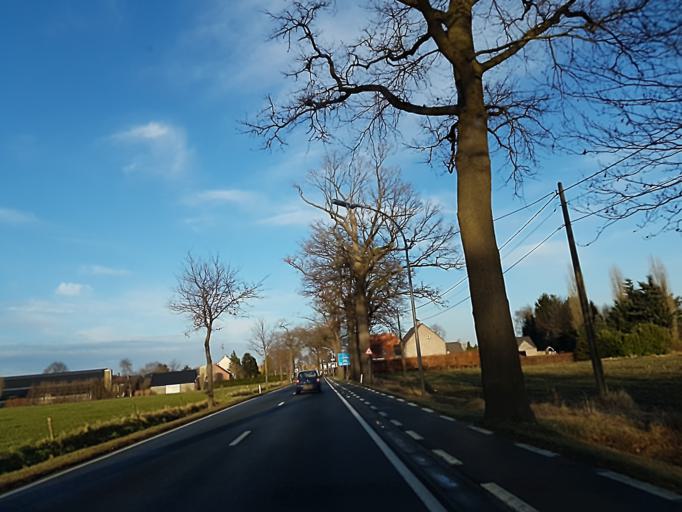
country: BE
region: Flanders
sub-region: Provincie Antwerpen
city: Ravels
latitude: 51.4053
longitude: 5.0081
